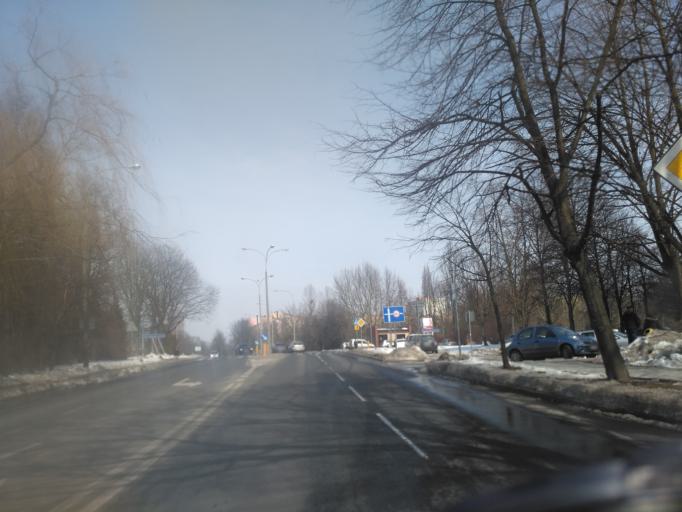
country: PL
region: Lublin Voivodeship
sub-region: Powiat lubelski
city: Lublin
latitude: 51.2614
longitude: 22.5414
